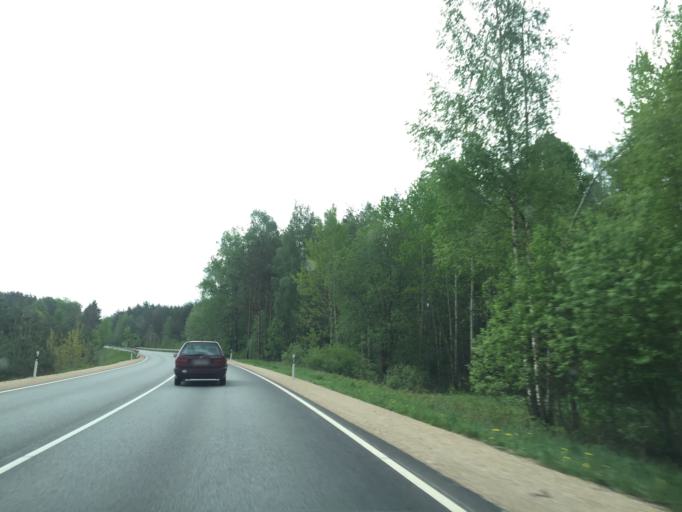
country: LV
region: Ikskile
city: Ikskile
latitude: 56.8922
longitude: 24.4524
